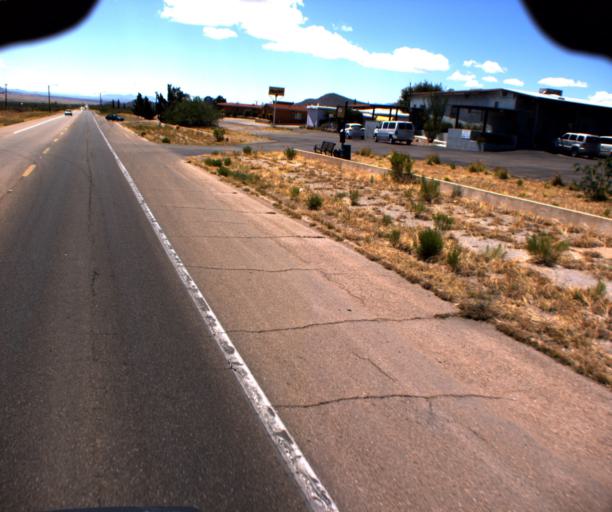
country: US
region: Arizona
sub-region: Cochise County
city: Bisbee
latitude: 31.3965
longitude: -109.9294
